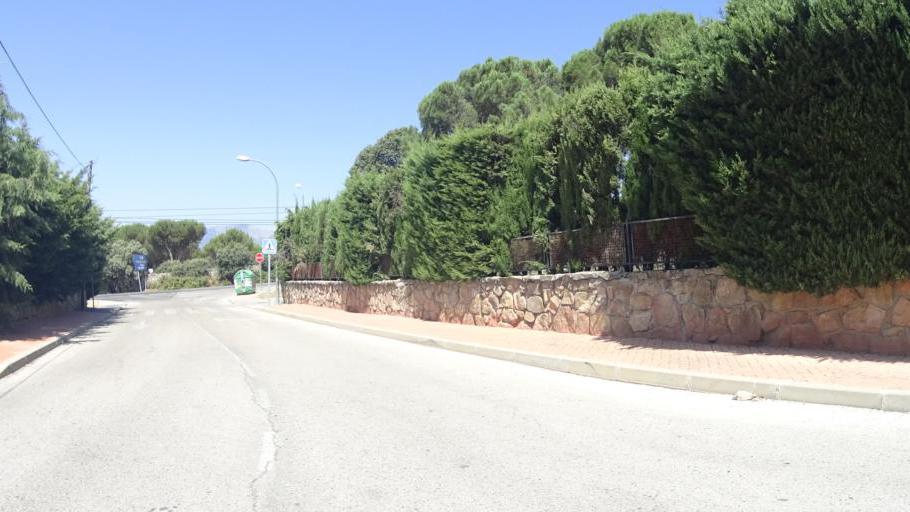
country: ES
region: Madrid
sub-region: Provincia de Madrid
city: Colmenarejo
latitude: 40.5675
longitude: -4.0120
